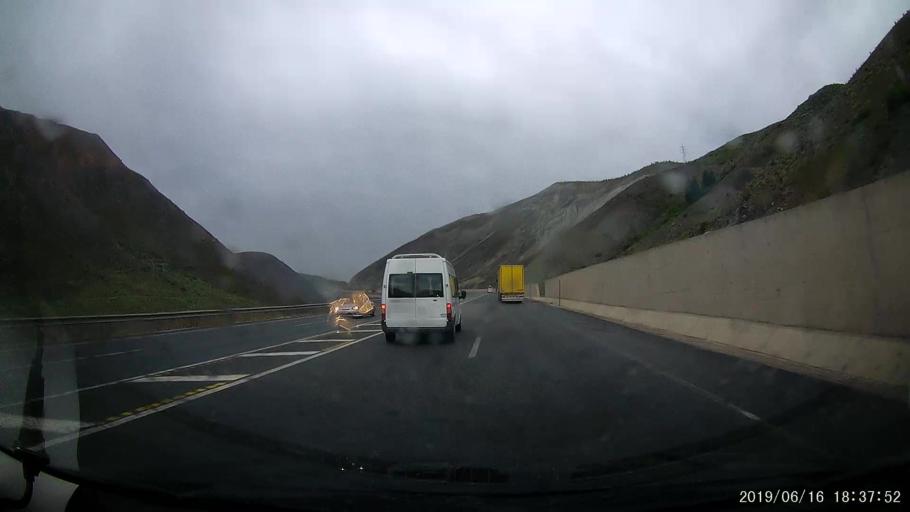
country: TR
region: Erzincan
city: Catalarmut
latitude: 39.8848
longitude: 39.1909
